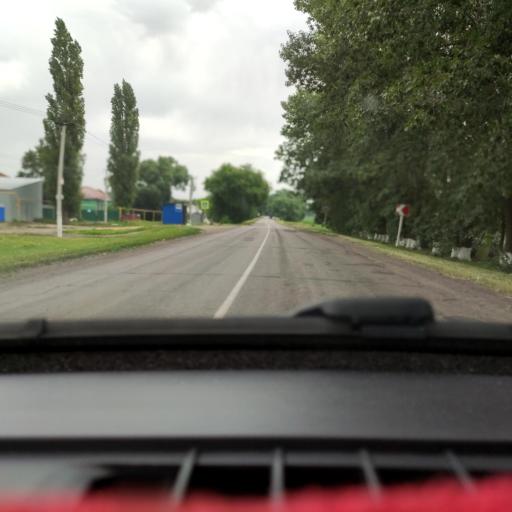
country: RU
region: Voronezj
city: Davydovka
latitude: 51.2448
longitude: 39.5629
